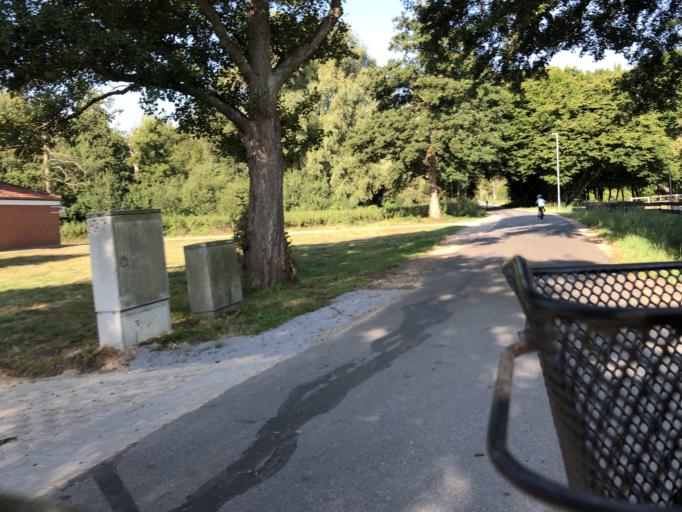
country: DE
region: Lower Saxony
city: Dahlenburg
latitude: 53.1854
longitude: 10.7413
